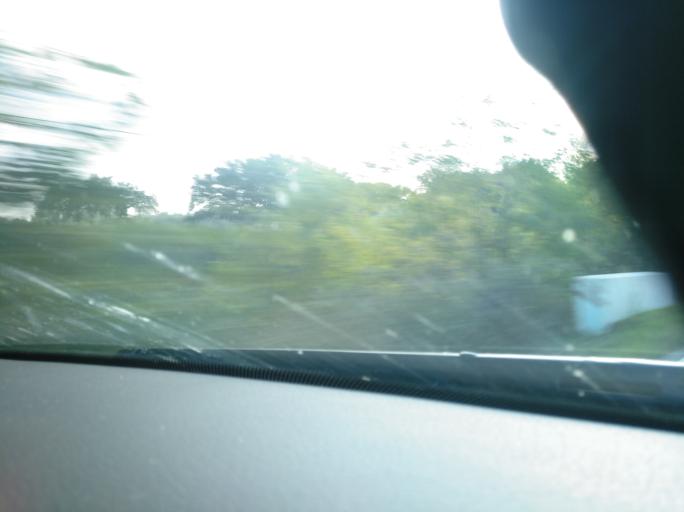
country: PT
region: Portalegre
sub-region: Fronteira
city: Fronteira
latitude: 38.9588
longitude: -7.6293
